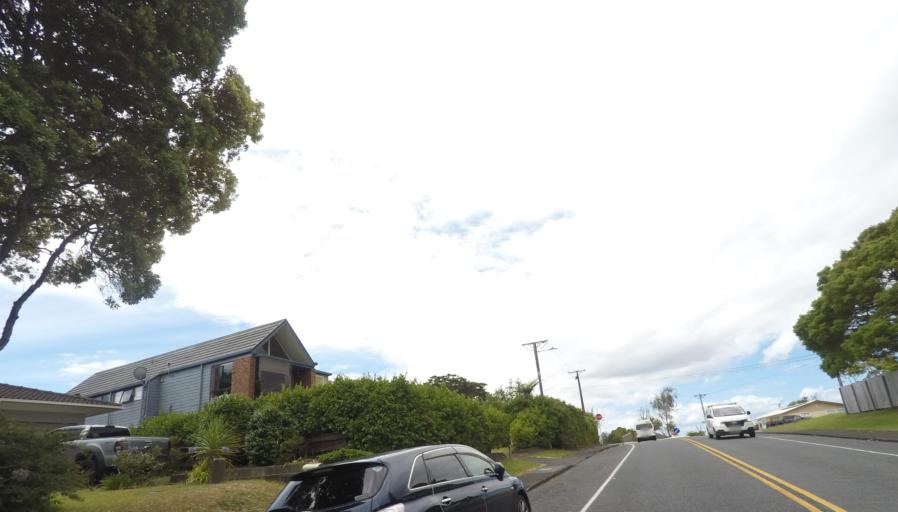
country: NZ
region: Auckland
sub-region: Auckland
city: Rosebank
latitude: -36.8464
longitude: 174.6148
